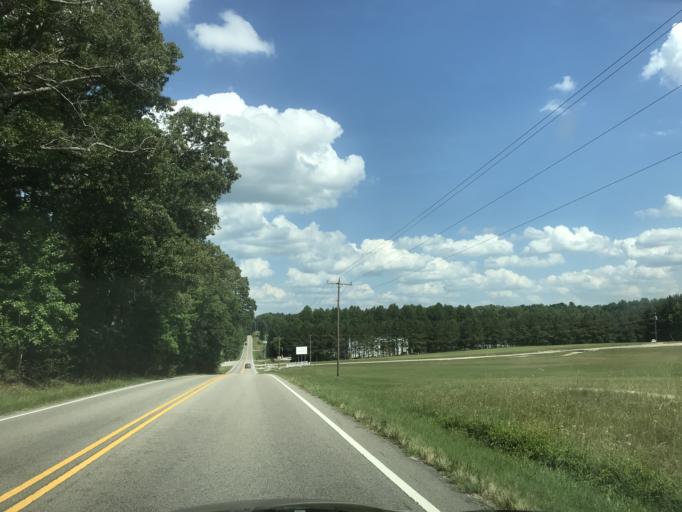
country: US
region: North Carolina
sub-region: Franklin County
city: Louisburg
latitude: 35.9645
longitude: -78.3108
